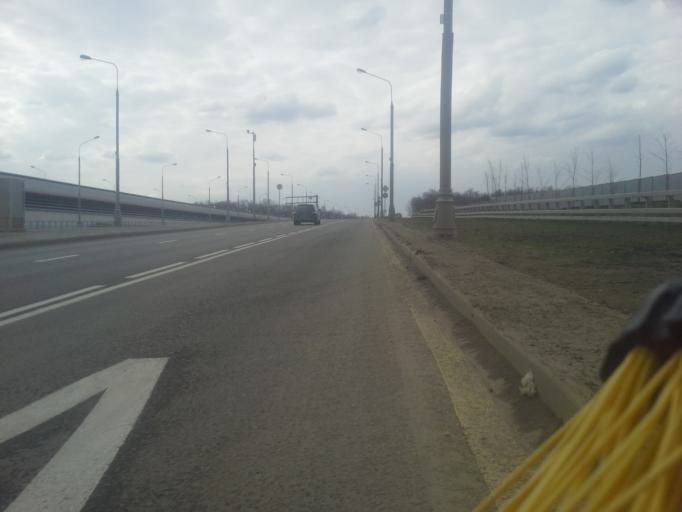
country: RU
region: Moskovskaya
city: Mosrentgen
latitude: 55.5886
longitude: 37.4283
